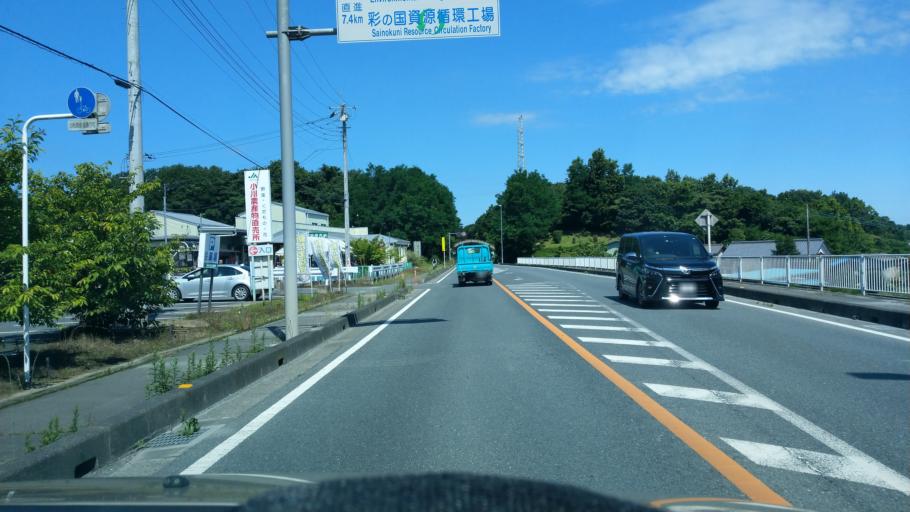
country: JP
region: Saitama
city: Ogawa
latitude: 36.0679
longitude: 139.2859
